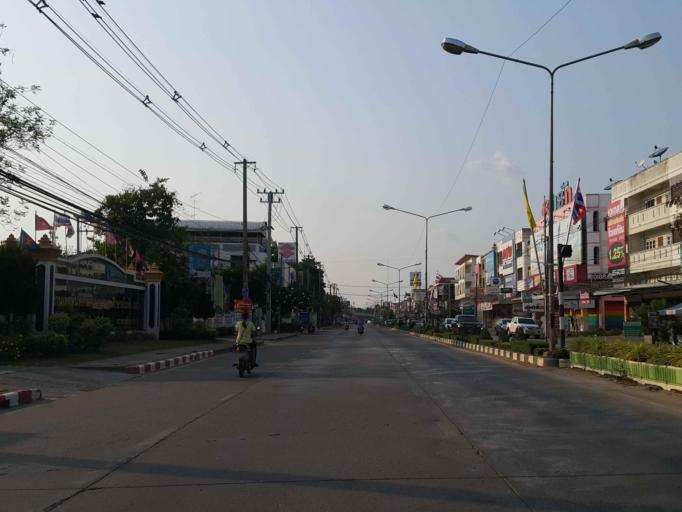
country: TH
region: Sukhothai
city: Sawankhalok
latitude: 17.3071
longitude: 99.8321
